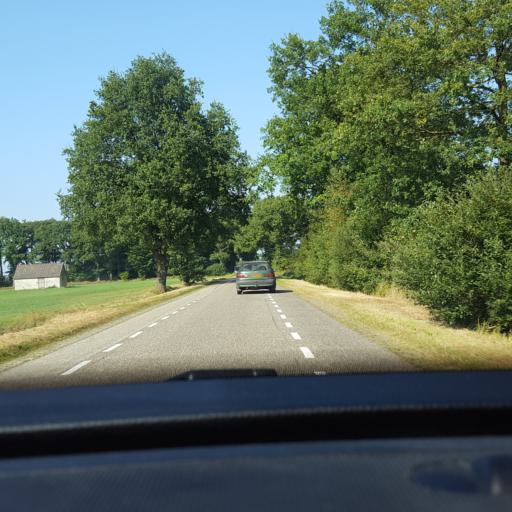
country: NL
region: Gelderland
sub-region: Gemeente Lochem
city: Barchem
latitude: 52.0580
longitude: 6.4536
